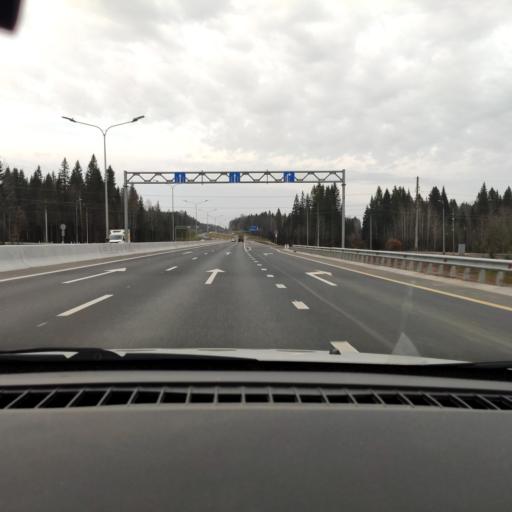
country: RU
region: Perm
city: Novyye Lyady
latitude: 58.0878
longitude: 56.4286
